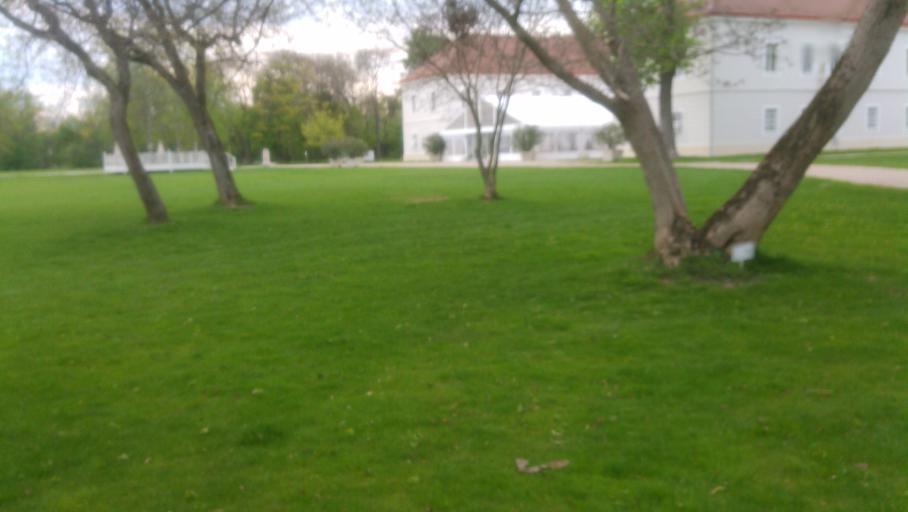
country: SK
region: Bratislavsky
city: Dunajska Luzna
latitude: 48.1375
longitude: 17.3237
